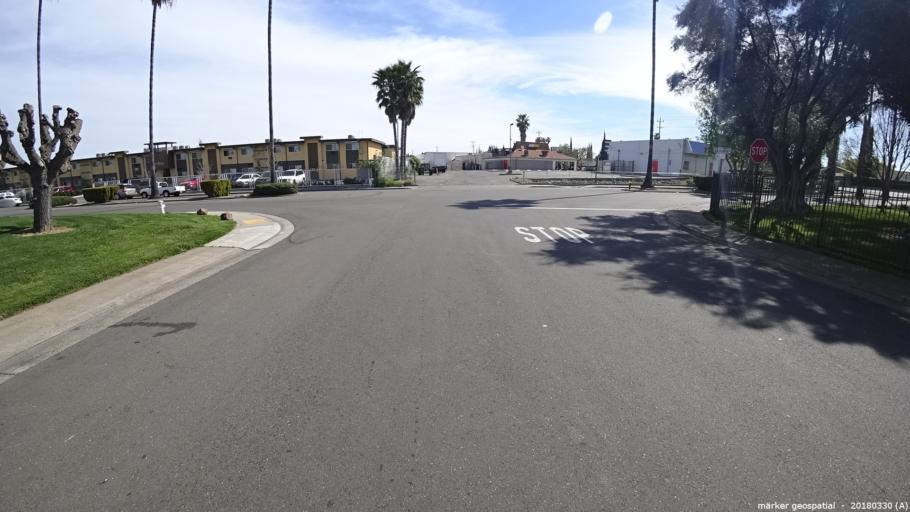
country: US
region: California
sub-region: Sacramento County
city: Rosemont
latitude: 38.5574
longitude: -121.3686
